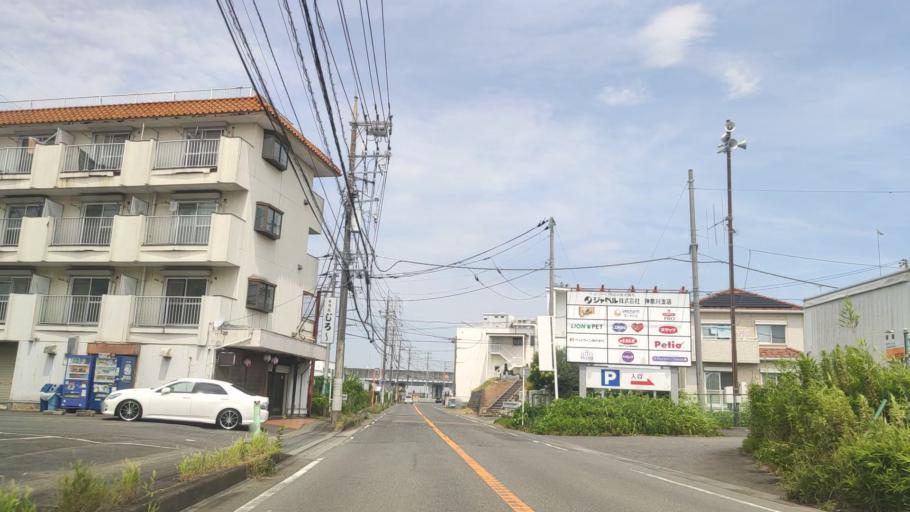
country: JP
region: Kanagawa
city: Atsugi
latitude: 35.4242
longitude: 139.3944
